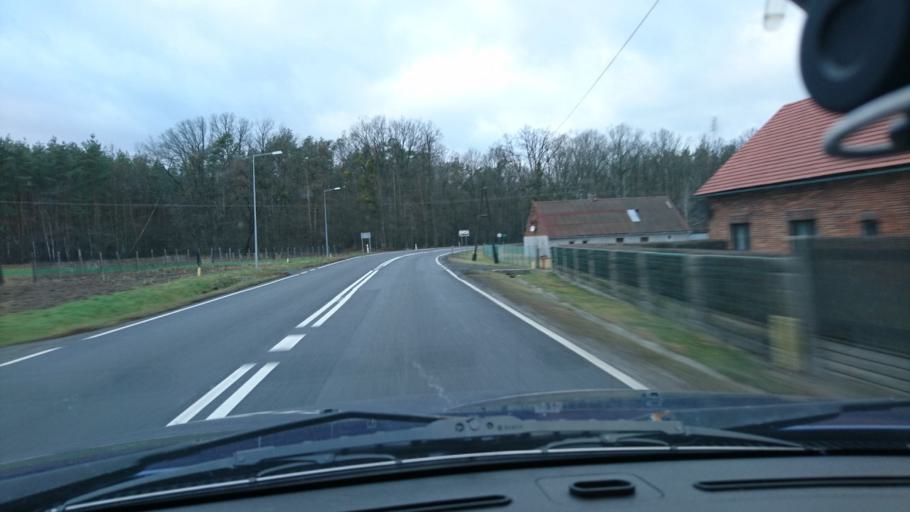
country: PL
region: Opole Voivodeship
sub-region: Powiat kluczborski
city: Kluczbork
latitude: 50.9473
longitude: 18.3165
